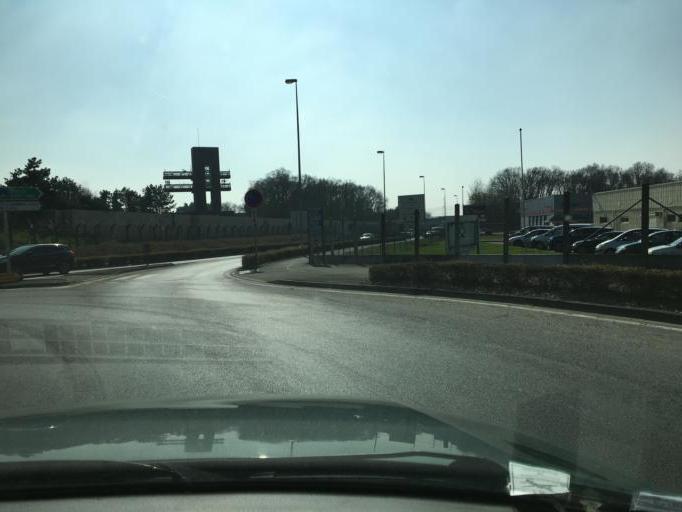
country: FR
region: Centre
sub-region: Departement du Loiret
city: Fleury-les-Aubrais
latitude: 47.9458
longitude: 1.9081
